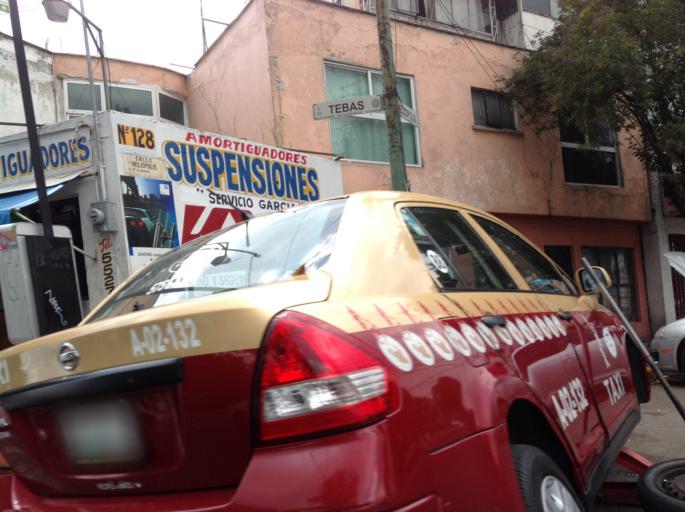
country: MX
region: Mexico City
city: Azcapotzalco
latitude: 19.4690
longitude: -99.1842
